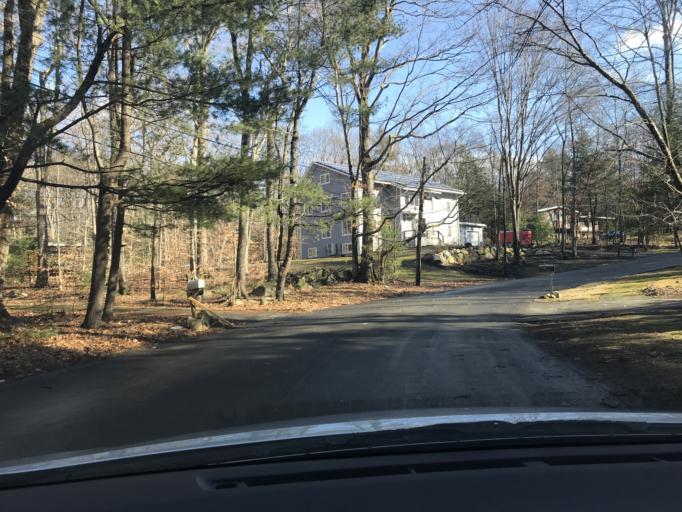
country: US
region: Massachusetts
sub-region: Middlesex County
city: Lexington
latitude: 42.4793
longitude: -71.2298
